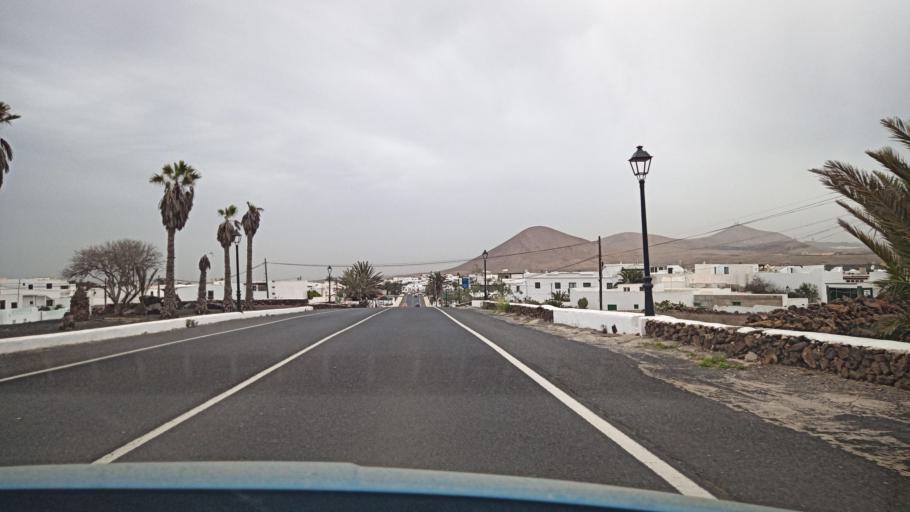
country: ES
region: Canary Islands
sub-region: Provincia de Las Palmas
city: Nazaret
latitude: 29.0167
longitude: -13.5422
